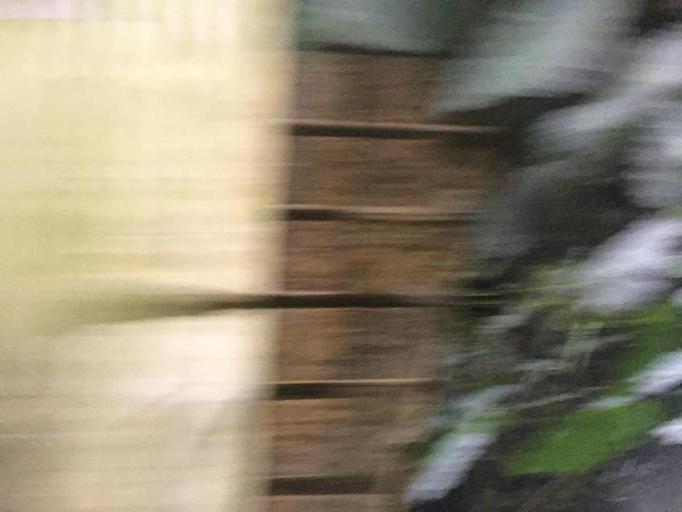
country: TW
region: Taiwan
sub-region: Chiayi
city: Jiayi Shi
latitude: 23.5246
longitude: 120.6515
